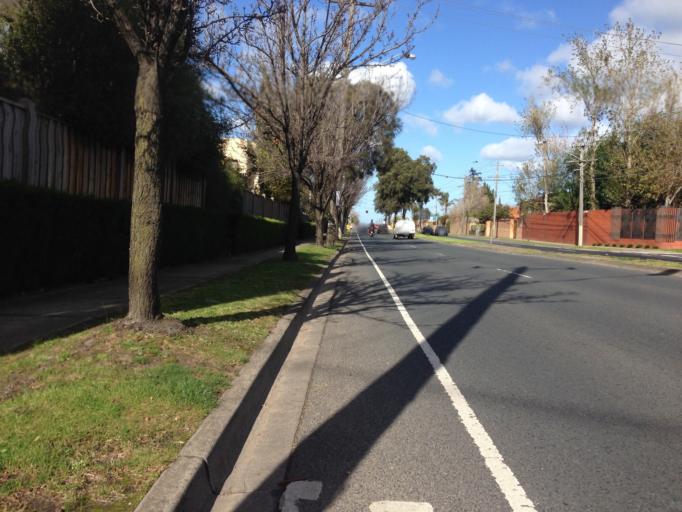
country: AU
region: Victoria
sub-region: Darebin
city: Preston
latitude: -37.7631
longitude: 145.0209
